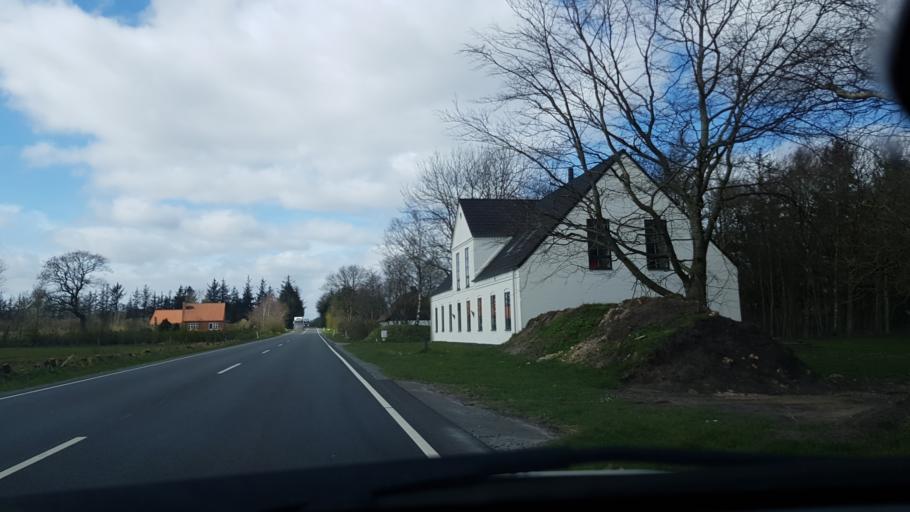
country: DK
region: South Denmark
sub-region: Esbjerg Kommune
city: Ribe
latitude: 55.2637
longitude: 8.8892
